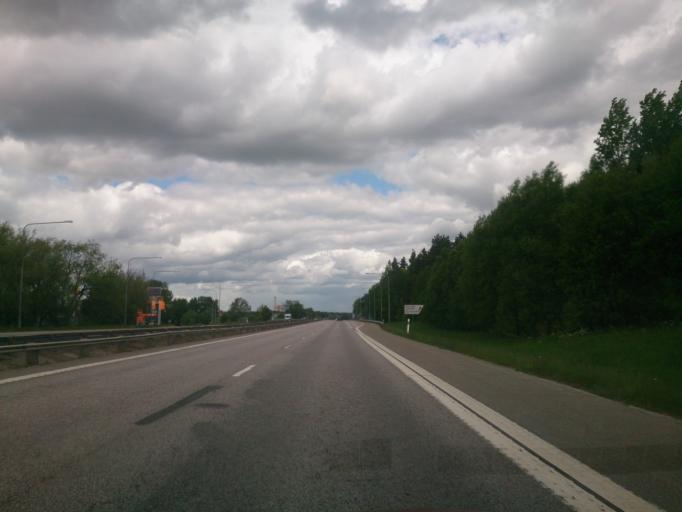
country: SE
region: OEstergoetland
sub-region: Norrkopings Kommun
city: Norrkoping
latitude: 58.5717
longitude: 16.2148
